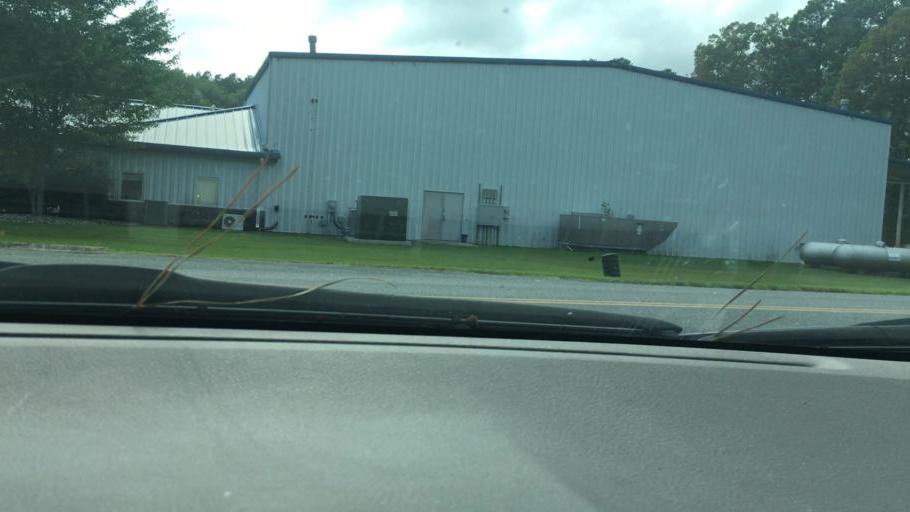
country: US
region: Maryland
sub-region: Worcester County
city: Pocomoke City
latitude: 38.0565
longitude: -75.5600
